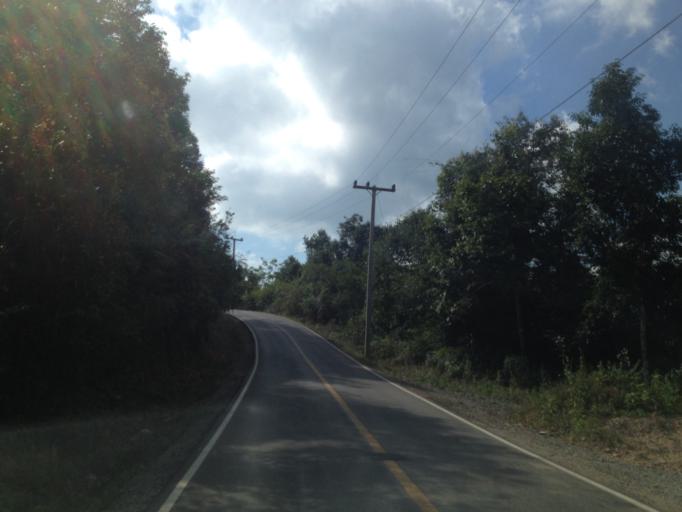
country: TH
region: Mae Hong Son
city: Ban Huai I Huak
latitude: 18.1452
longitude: 98.1358
